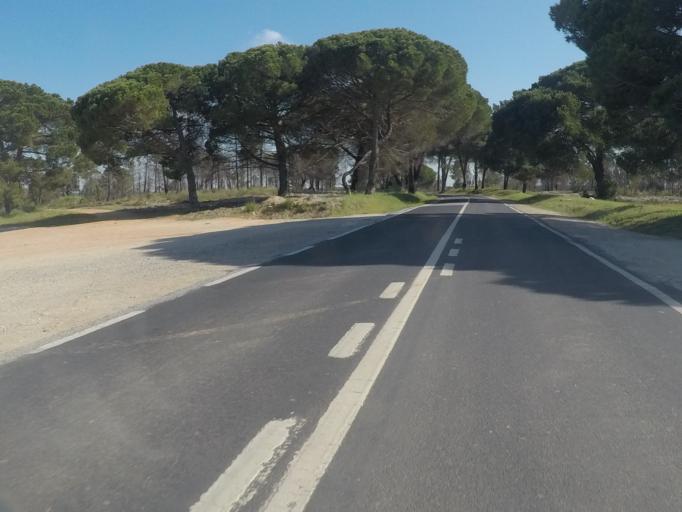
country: PT
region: Setubal
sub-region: Sesimbra
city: Sesimbra
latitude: 38.5165
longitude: -9.1439
